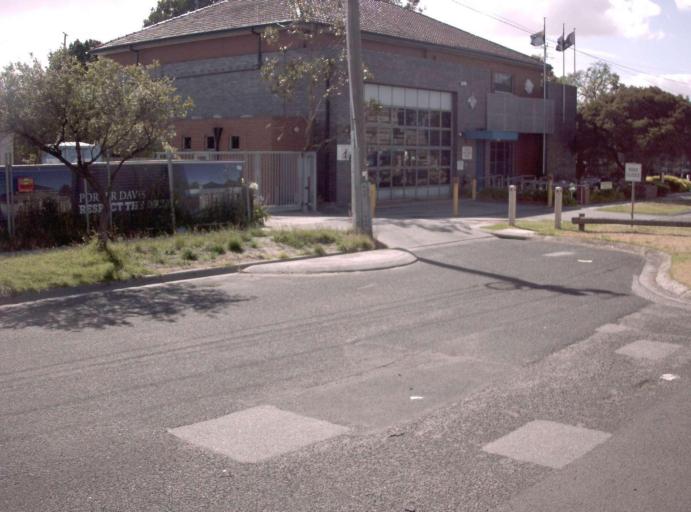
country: AU
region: Victoria
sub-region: Kingston
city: Mentone
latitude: -37.9810
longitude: 145.0703
